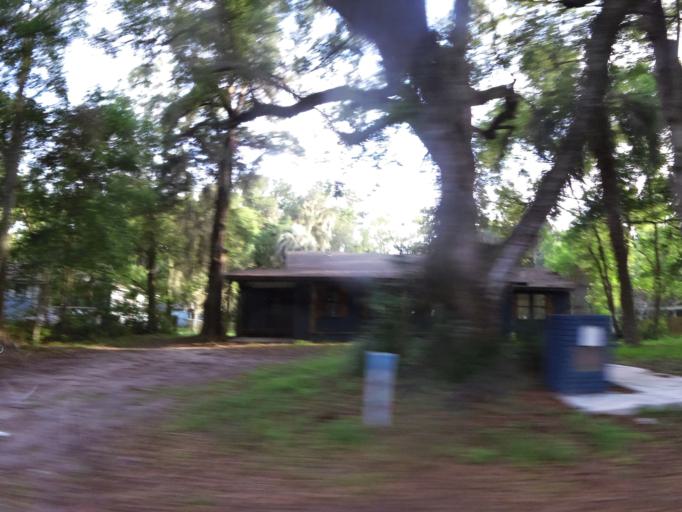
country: US
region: Florida
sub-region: Duval County
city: Jacksonville
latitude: 30.4163
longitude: -81.7039
